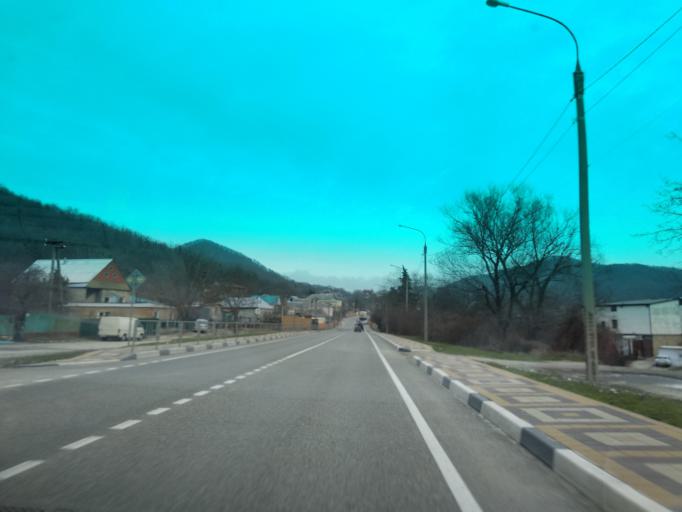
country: RU
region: Krasnodarskiy
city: Ol'ginka
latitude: 44.2080
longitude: 38.8915
